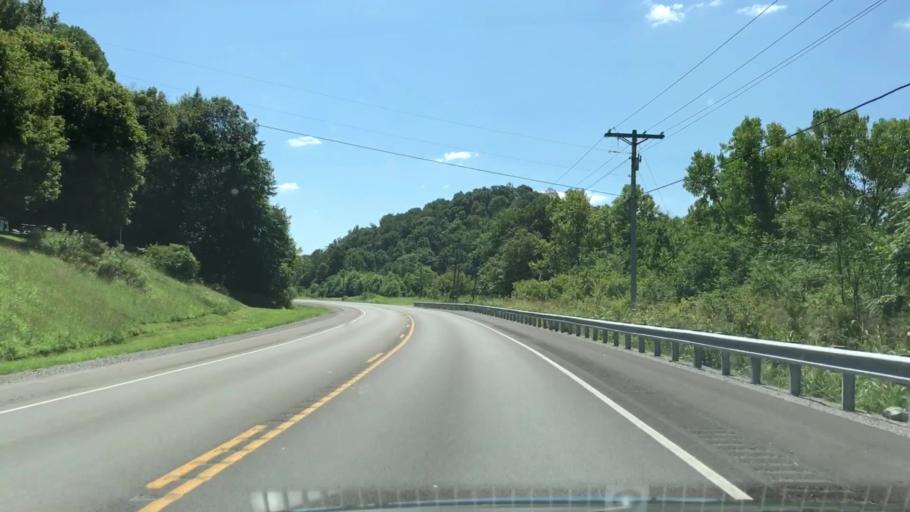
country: US
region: Kentucky
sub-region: Cumberland County
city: Burkesville
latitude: 36.7275
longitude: -85.3719
